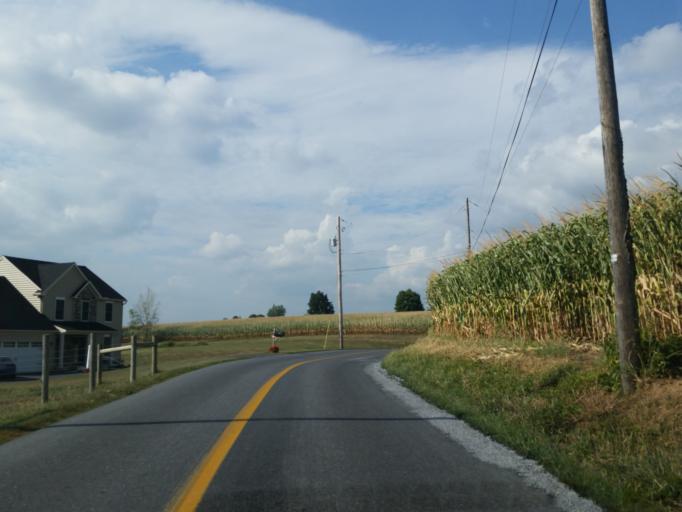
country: US
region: Pennsylvania
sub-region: Lancaster County
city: Manheim
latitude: 40.1689
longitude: -76.4564
